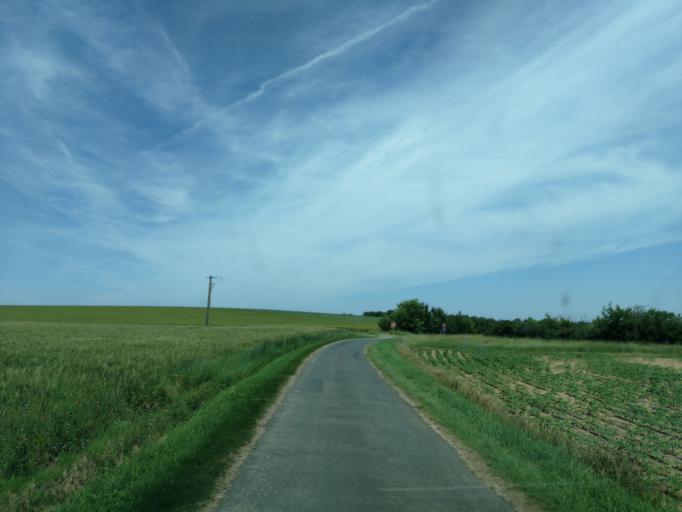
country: FR
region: Pays de la Loire
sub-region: Departement de la Vendee
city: Le Langon
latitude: 46.4254
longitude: -0.8947
